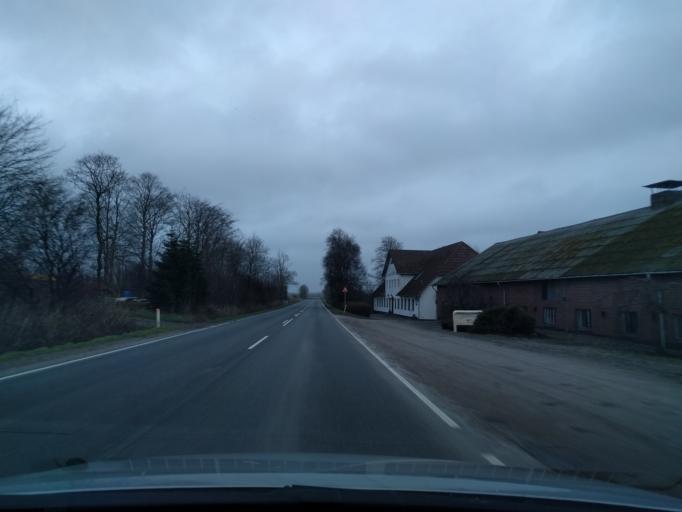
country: DK
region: South Denmark
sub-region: Tonder Kommune
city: Toftlund
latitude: 55.2504
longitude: 9.1685
